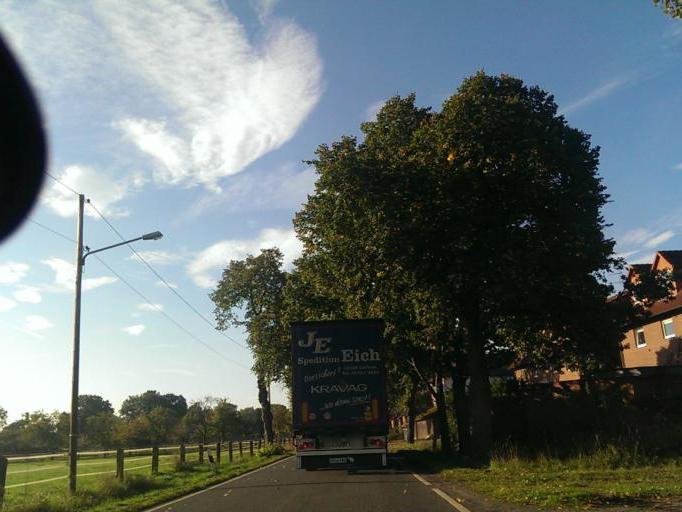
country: DE
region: Lower Saxony
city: Garbsen-Mitte
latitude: 52.4708
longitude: 9.6191
